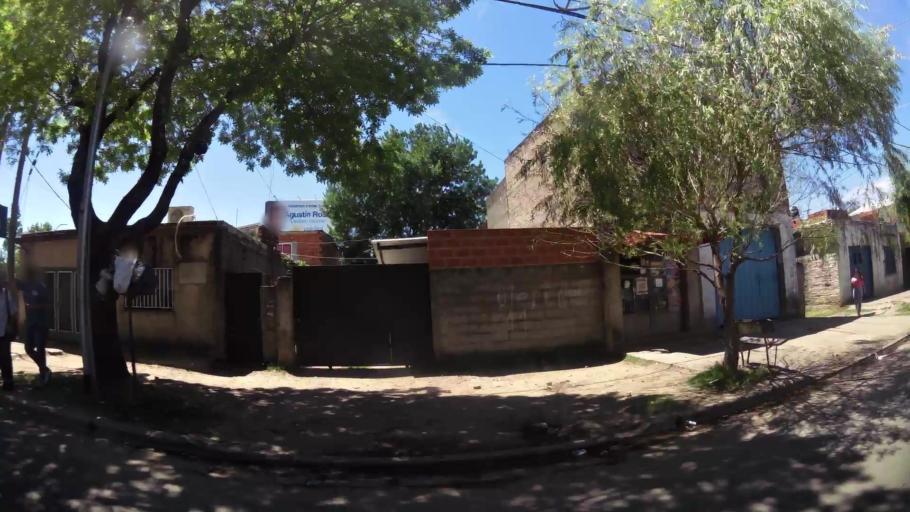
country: AR
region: Santa Fe
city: Perez
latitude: -32.9492
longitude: -60.7191
